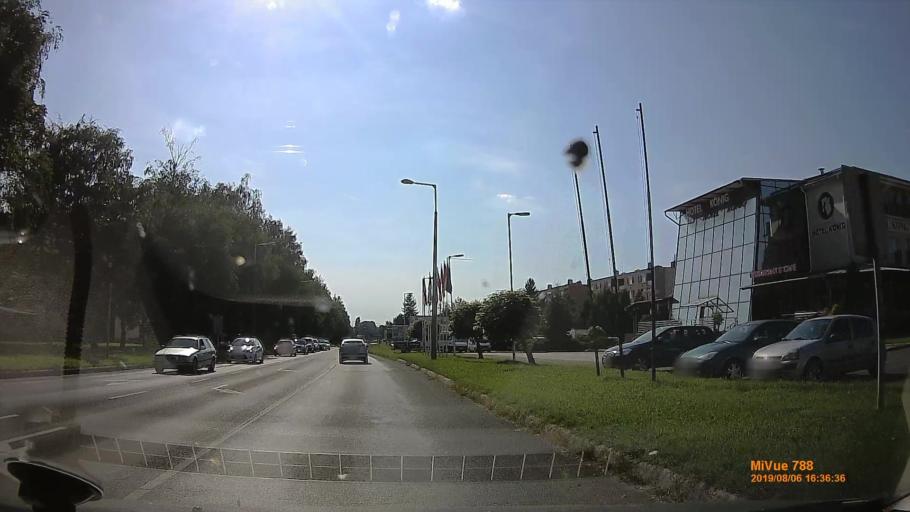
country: HU
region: Zala
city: Nagykanizsa
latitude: 46.4671
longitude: 16.9912
